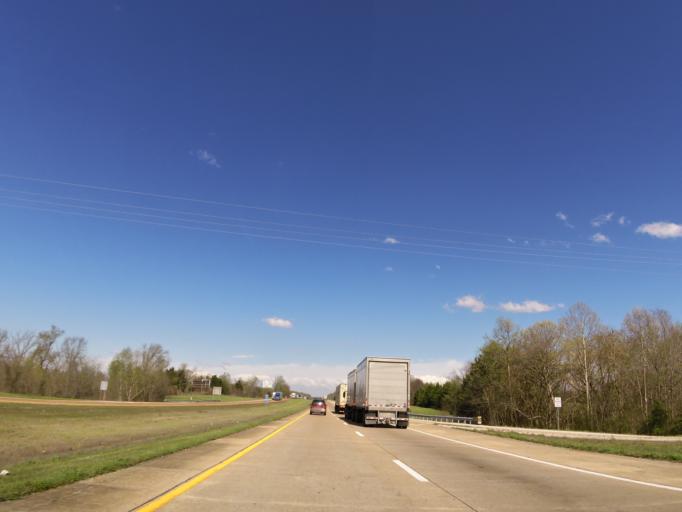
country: US
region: Tennessee
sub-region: Gibson County
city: Medina
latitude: 35.7186
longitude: -88.6323
